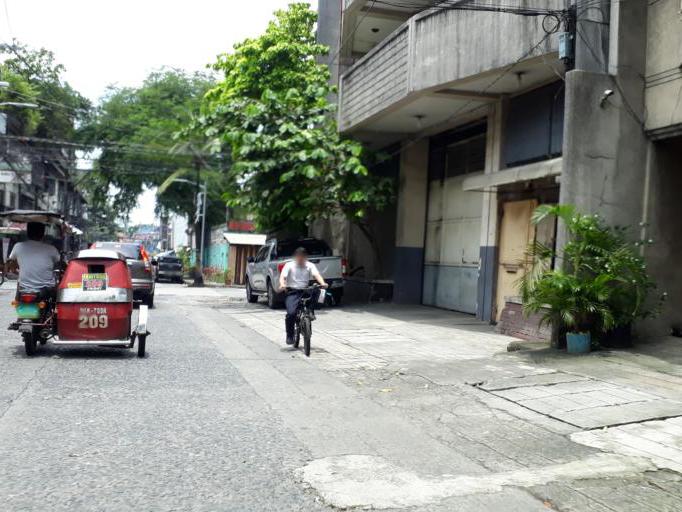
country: PH
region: Metro Manila
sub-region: Caloocan City
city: Niugan
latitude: 14.6461
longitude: 120.9798
